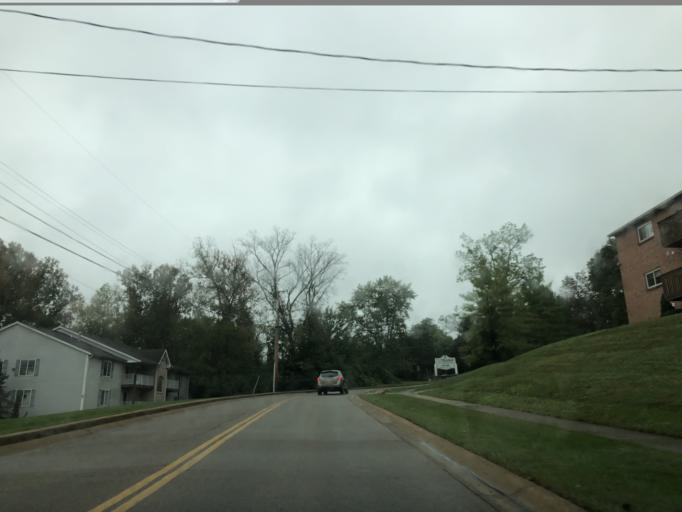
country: US
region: Ohio
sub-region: Hamilton County
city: Loveland
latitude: 39.2656
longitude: -84.2689
